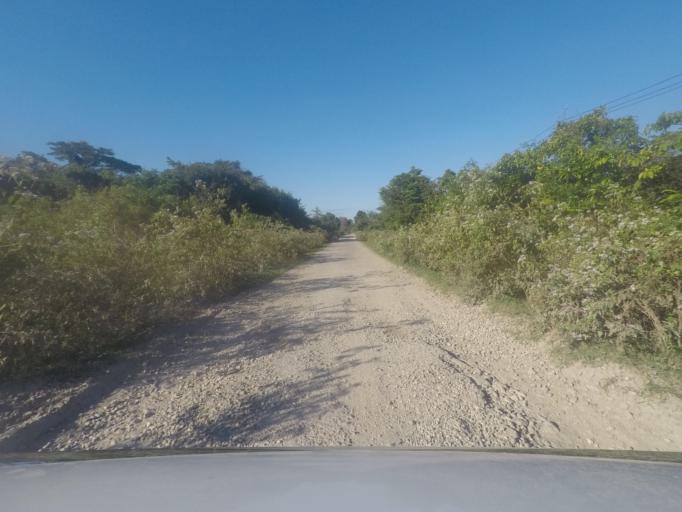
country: TL
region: Lautem
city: Lospalos
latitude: -8.4089
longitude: 127.1685
